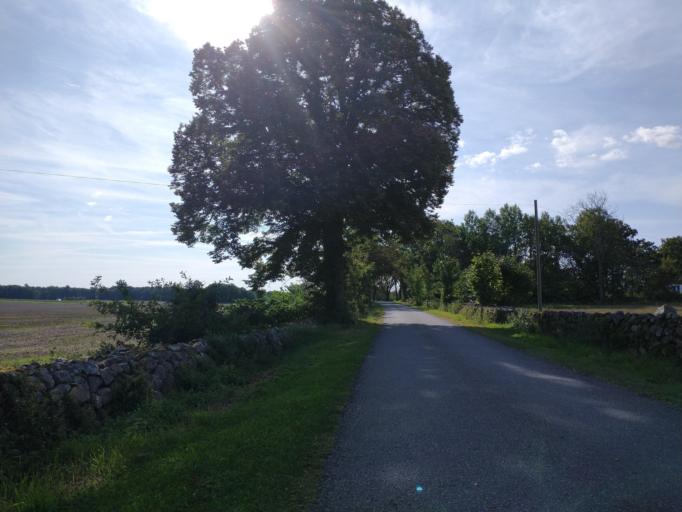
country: SE
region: Kalmar
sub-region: Kalmar Kommun
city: Lindsdal
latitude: 56.7783
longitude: 16.3229
